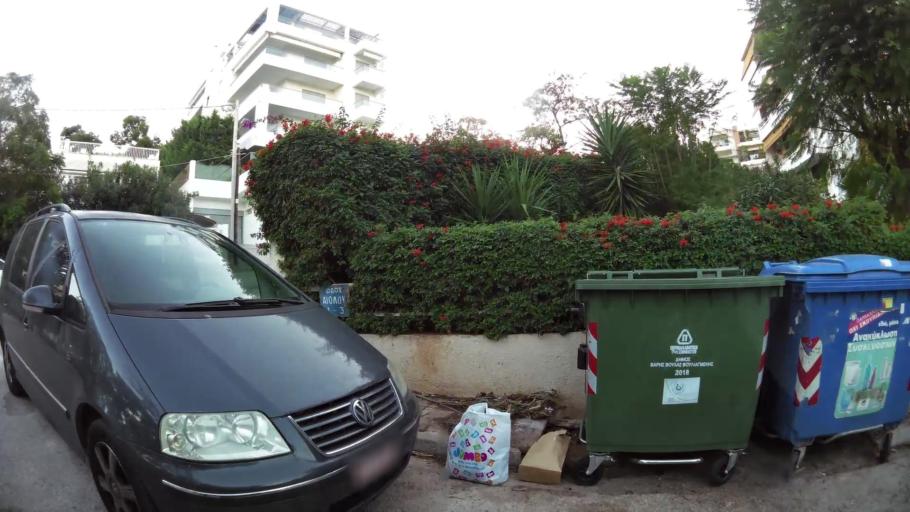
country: GR
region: Attica
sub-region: Nomarchia Anatolikis Attikis
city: Vouliagmeni
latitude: 37.8124
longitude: 23.7976
